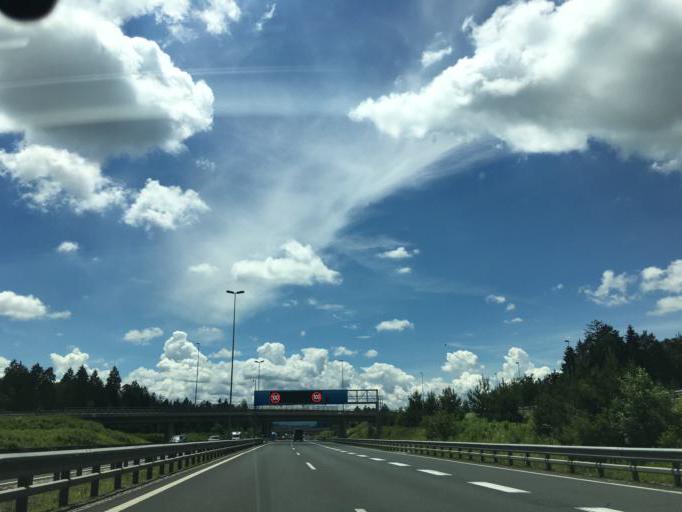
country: SI
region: Ljubljana
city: Ljubljana
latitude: 46.0721
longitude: 14.4589
